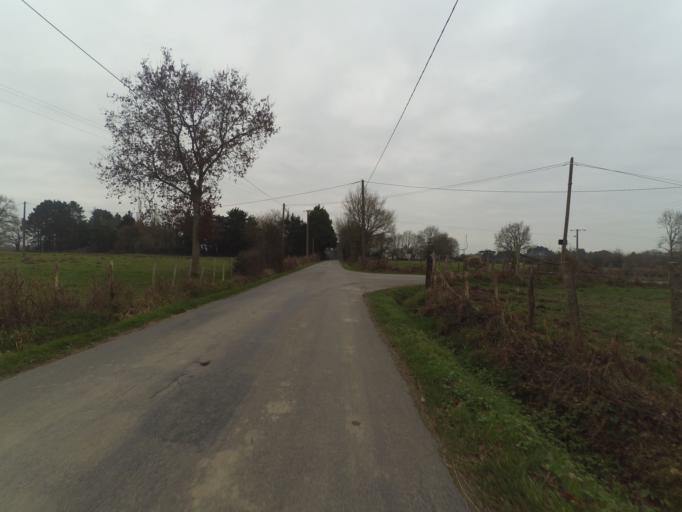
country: FR
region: Pays de la Loire
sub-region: Departement de la Loire-Atlantique
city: Sautron
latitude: 47.2558
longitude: -1.7074
